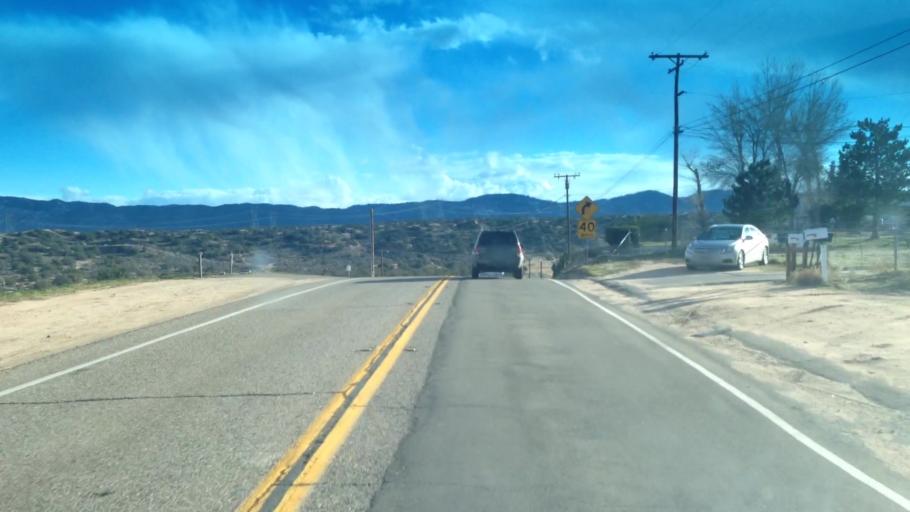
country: US
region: California
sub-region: San Bernardino County
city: Hesperia
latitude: 34.3740
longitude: -117.3144
